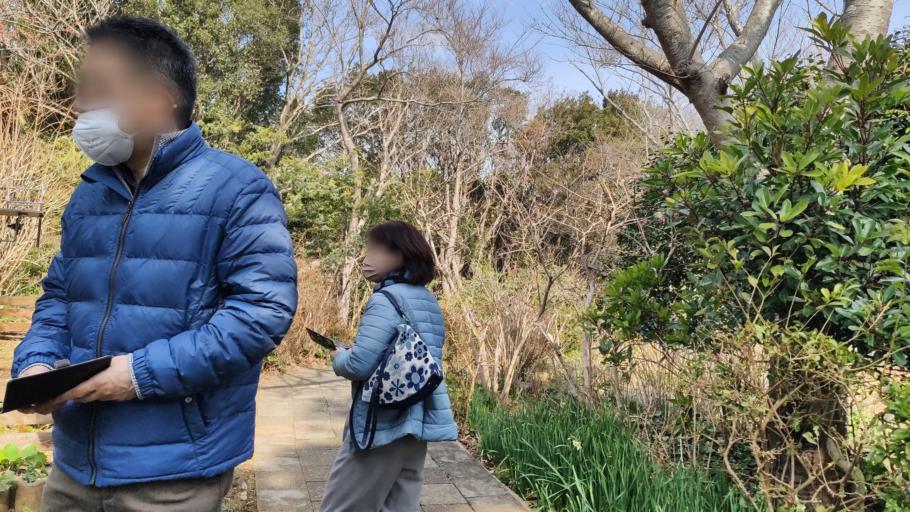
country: JP
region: Shizuoka
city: Shimoda
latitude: 34.6798
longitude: 138.9529
